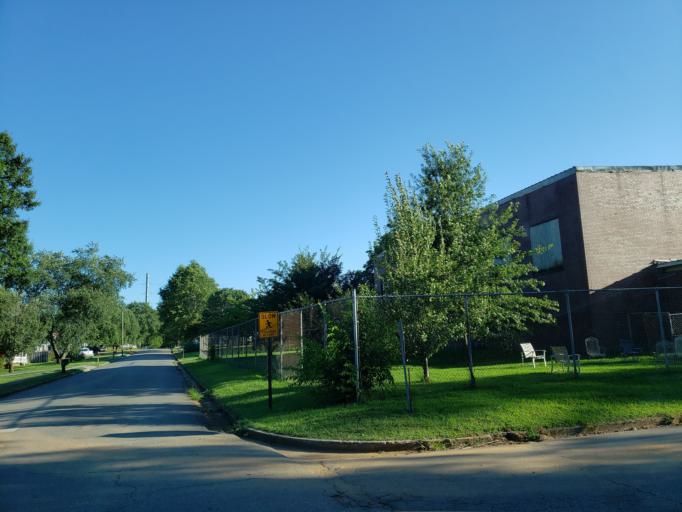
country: US
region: Georgia
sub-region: Polk County
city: Aragon
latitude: 34.0427
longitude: -85.0562
